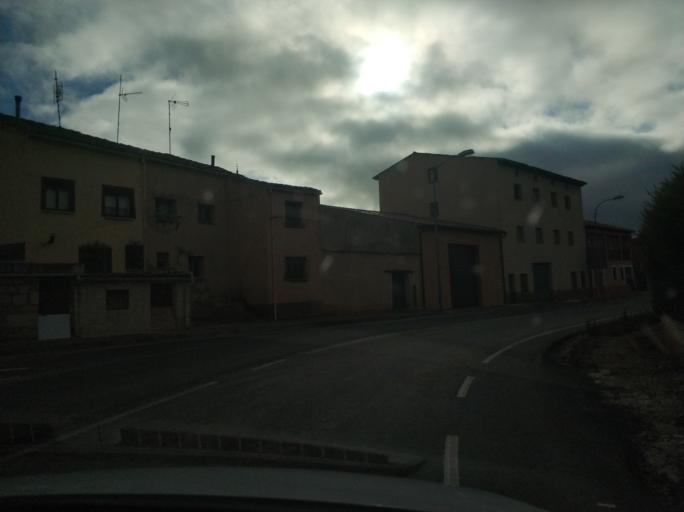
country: ES
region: Castille and Leon
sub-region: Provincia de Soria
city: San Esteban de Gormaz
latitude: 41.5762
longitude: -3.2083
